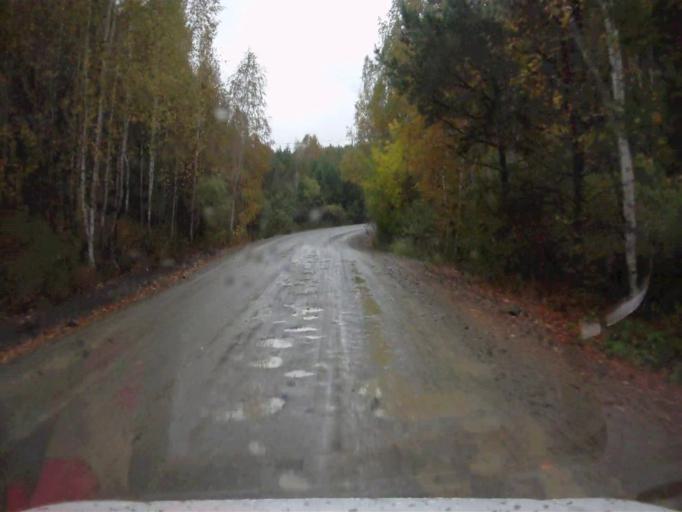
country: RU
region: Chelyabinsk
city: Kyshtym
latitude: 55.7473
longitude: 60.4904
